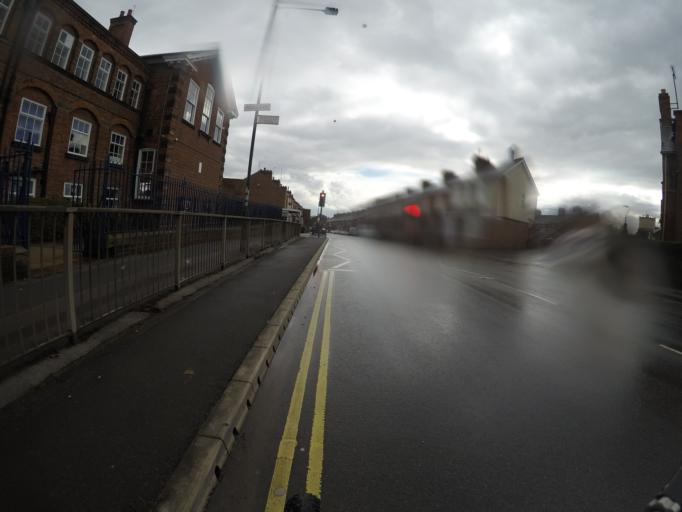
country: GB
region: England
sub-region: City of York
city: York
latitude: 53.9624
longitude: -1.1157
